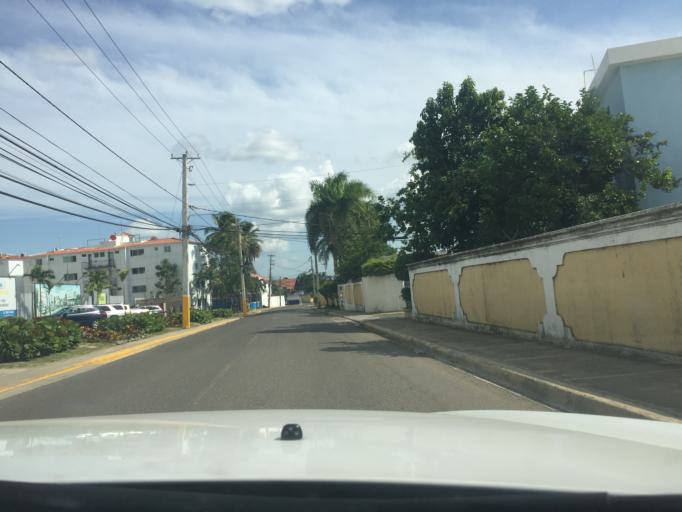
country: DO
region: Santiago
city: Tamboril
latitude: 19.4769
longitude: -70.6560
